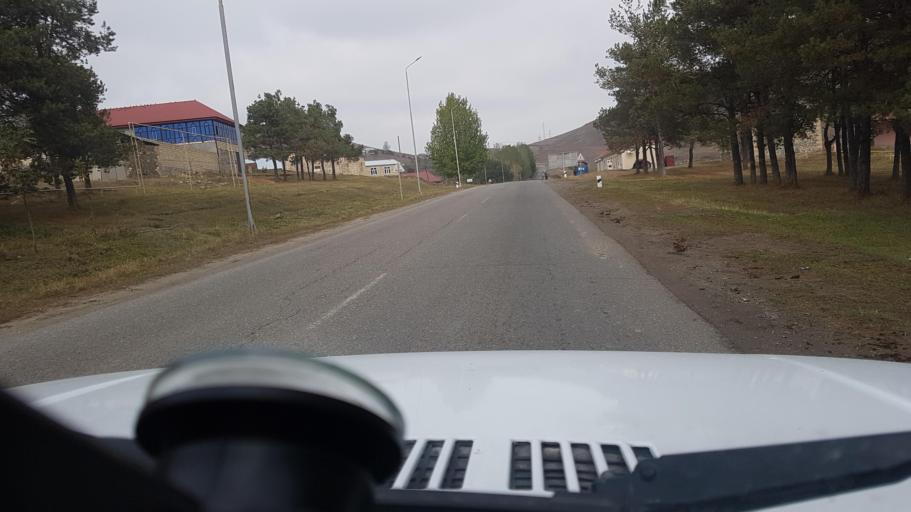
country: AZ
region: Gadabay Rayon
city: Ariqdam
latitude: 40.6054
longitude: 45.8124
